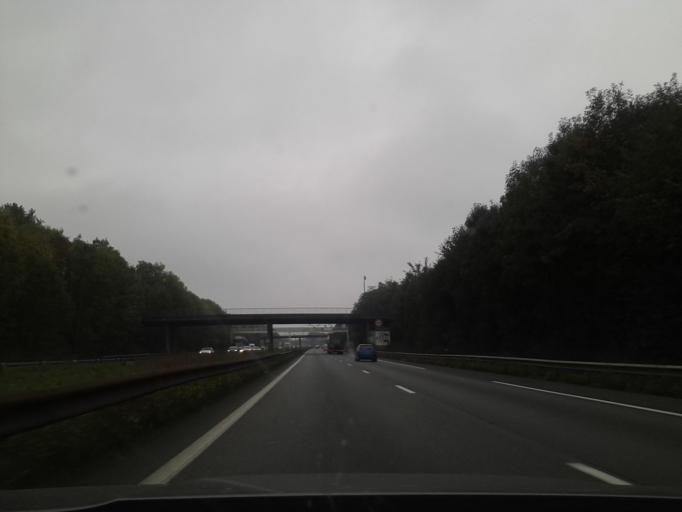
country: FR
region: Nord-Pas-de-Calais
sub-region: Departement du Nord
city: Aulnoy-lez-Valenciennes
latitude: 50.3388
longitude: 3.5289
